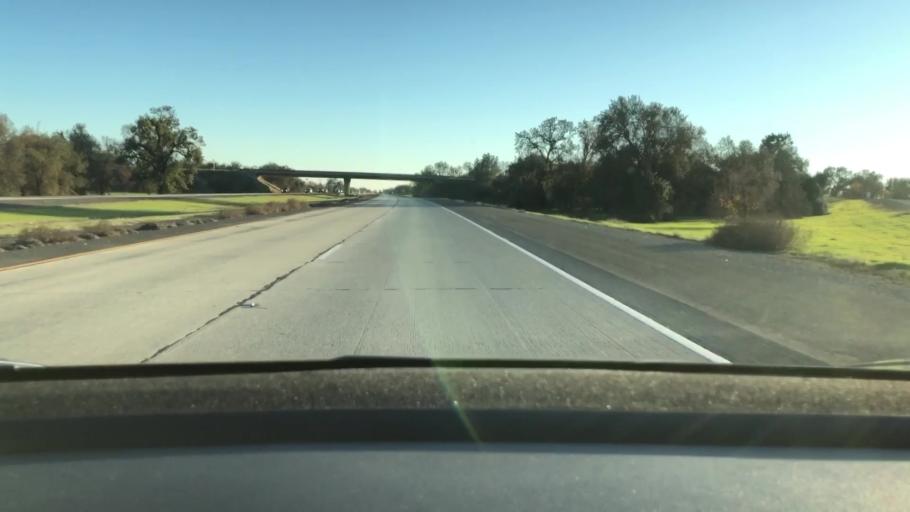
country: US
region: California
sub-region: Yolo County
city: Woodland
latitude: 38.6217
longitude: -121.7668
